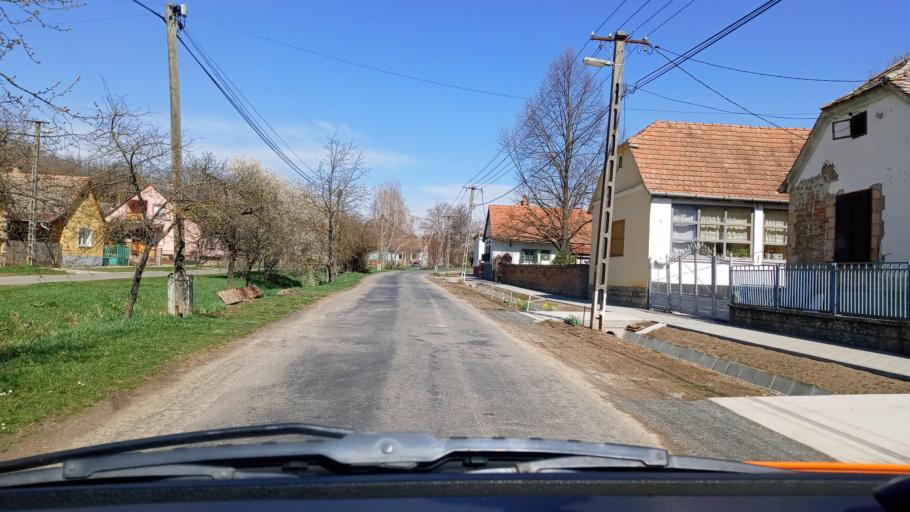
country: HU
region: Baranya
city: Pecsvarad
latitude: 46.0637
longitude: 18.4500
